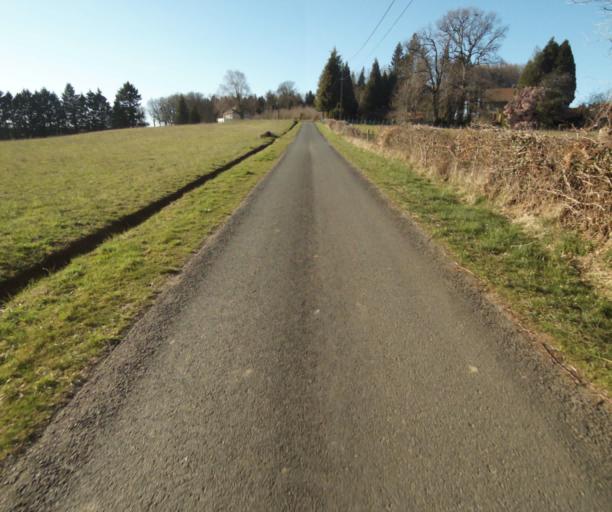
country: FR
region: Limousin
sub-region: Departement de la Correze
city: Seilhac
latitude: 45.3833
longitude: 1.7006
